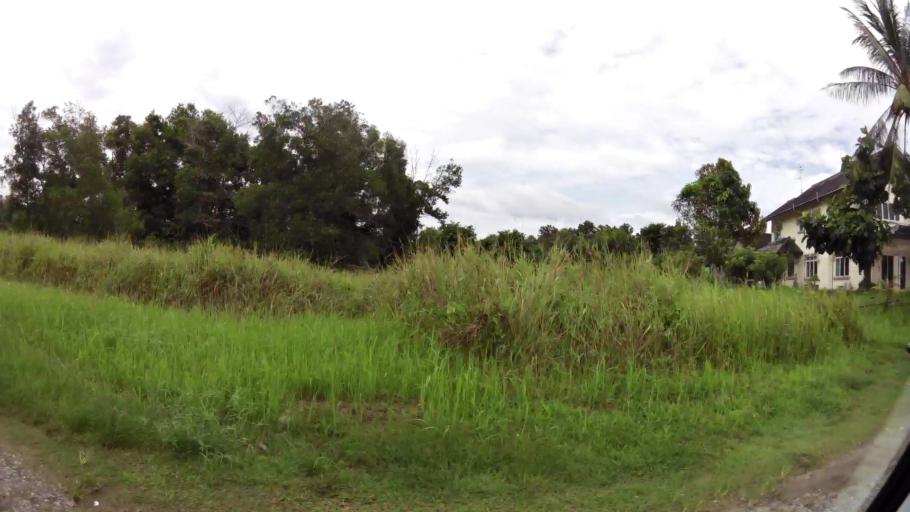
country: BN
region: Brunei and Muara
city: Bandar Seri Begawan
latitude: 4.8802
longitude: 114.8969
